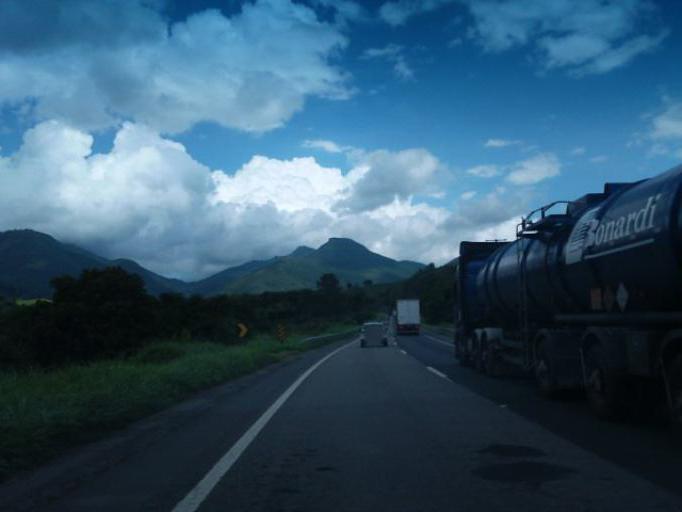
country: BR
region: Sao Paulo
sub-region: Cajati
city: Cajati
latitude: -24.7807
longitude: -48.1931
